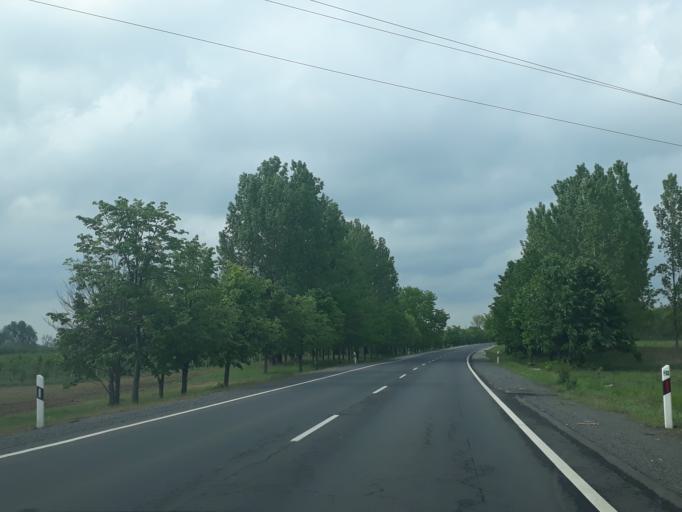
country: HU
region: Szabolcs-Szatmar-Bereg
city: Ajak
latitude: 48.1885
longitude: 22.0417
